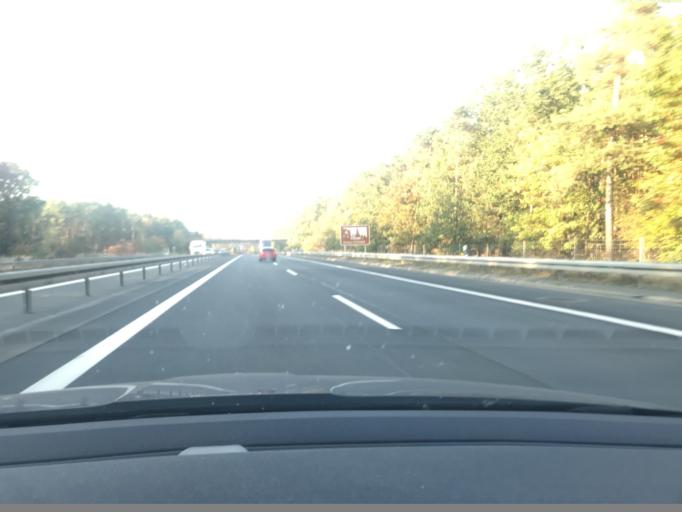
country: DE
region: Saxony
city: Radeburg
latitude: 51.2531
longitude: 13.7248
